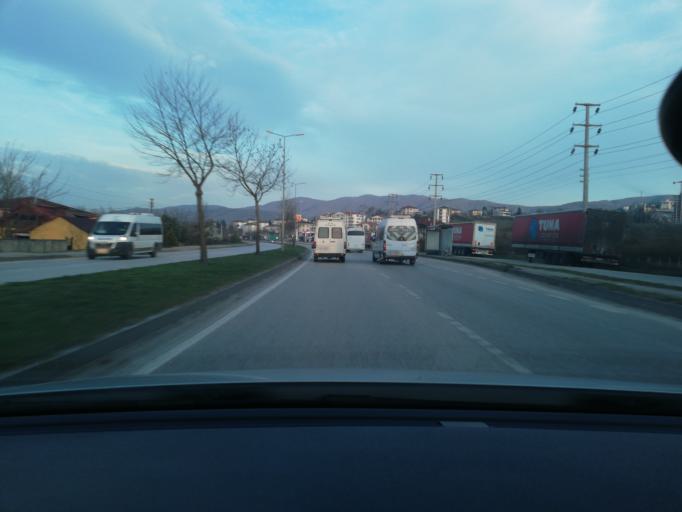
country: TR
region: Duzce
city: Konuralp
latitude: 40.8986
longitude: 31.1626
